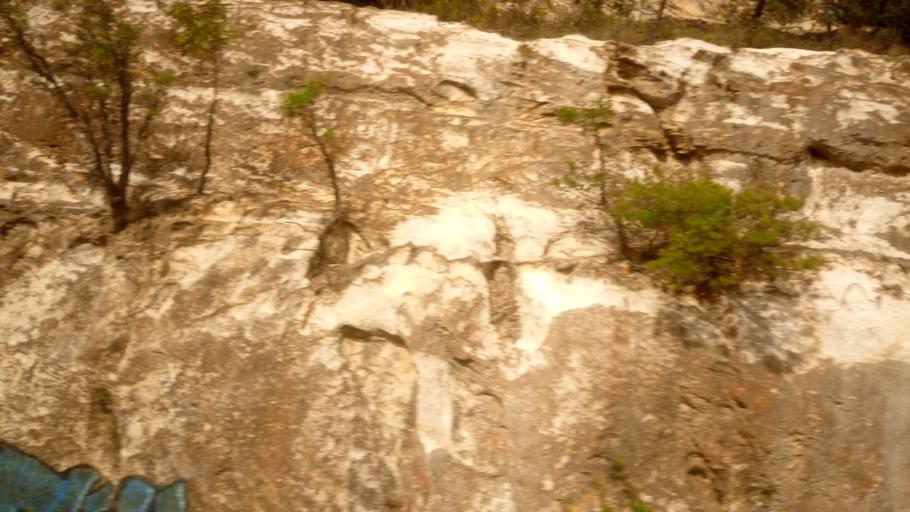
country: AU
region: New South Wales
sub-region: Blue Mountains Municipality
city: Lawson
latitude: -33.7178
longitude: 150.3857
